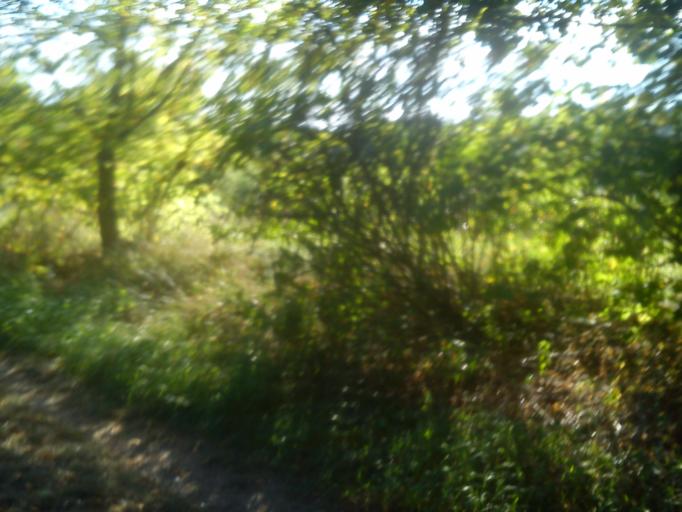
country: CZ
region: South Moravian
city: Sokolnice
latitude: 49.1096
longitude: 16.7653
